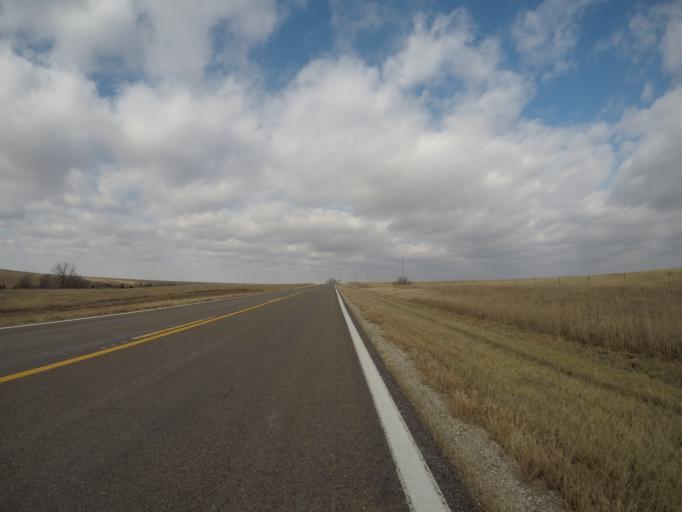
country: US
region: Kansas
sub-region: Wabaunsee County
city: Alma
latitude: 38.8629
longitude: -96.3725
